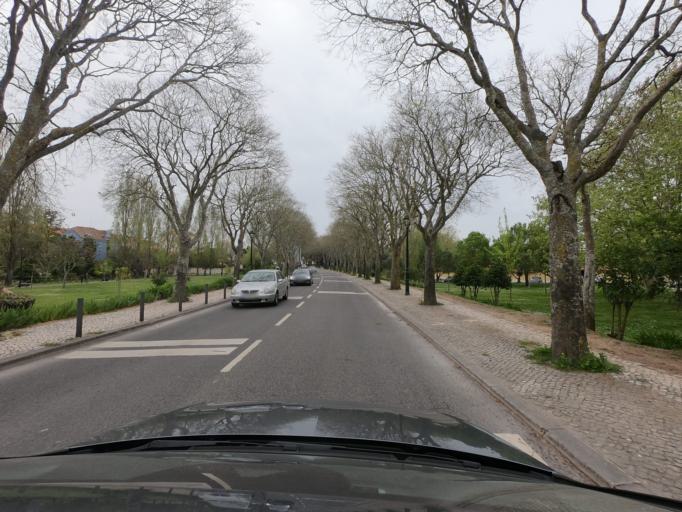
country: PT
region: Lisbon
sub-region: Sintra
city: Queluz
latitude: 38.7534
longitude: -9.2596
